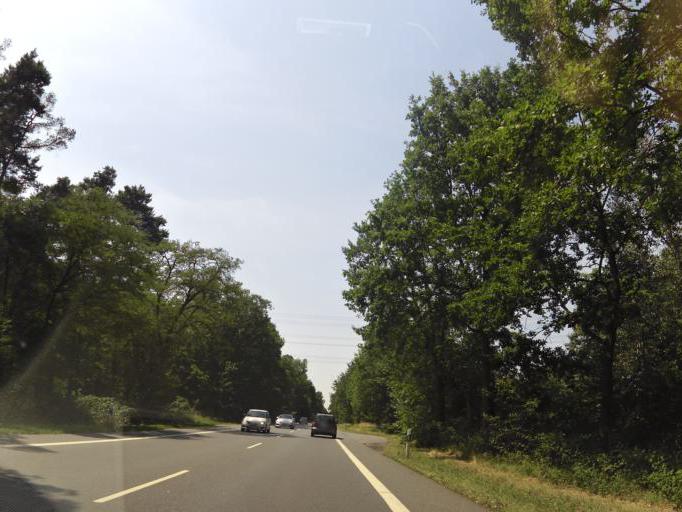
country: DE
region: Hesse
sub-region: Regierungsbezirk Darmstadt
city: Buttelborn
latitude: 49.9045
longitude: 8.5546
